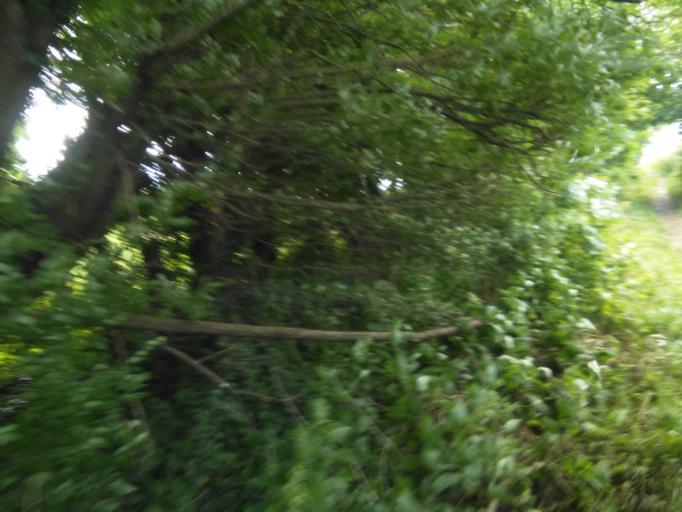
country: DK
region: Central Jutland
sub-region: Syddjurs Kommune
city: Ronde
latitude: 56.1999
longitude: 10.4418
